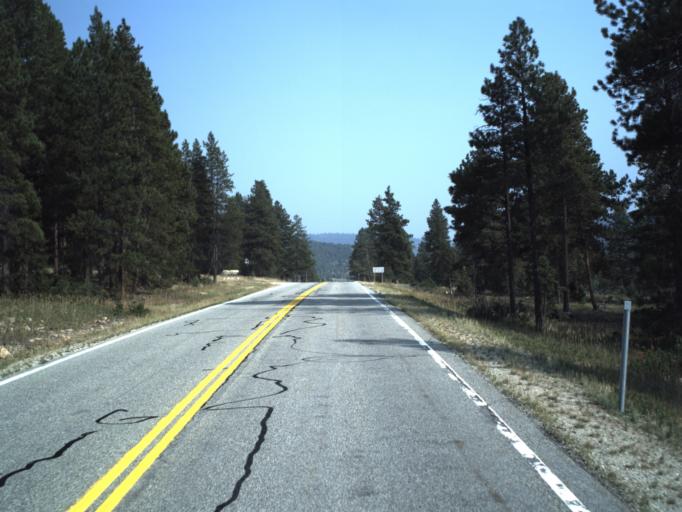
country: US
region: Utah
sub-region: Summit County
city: Kamas
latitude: 40.6297
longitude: -111.1765
